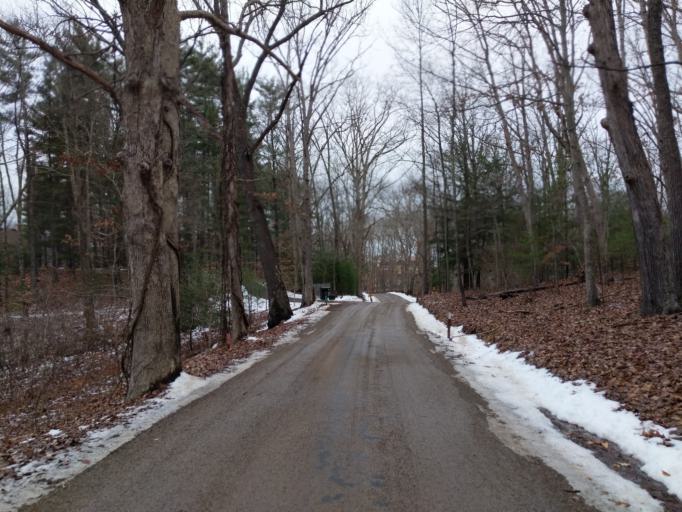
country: US
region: Ohio
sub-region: Athens County
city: The Plains
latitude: 39.3251
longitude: -82.1516
